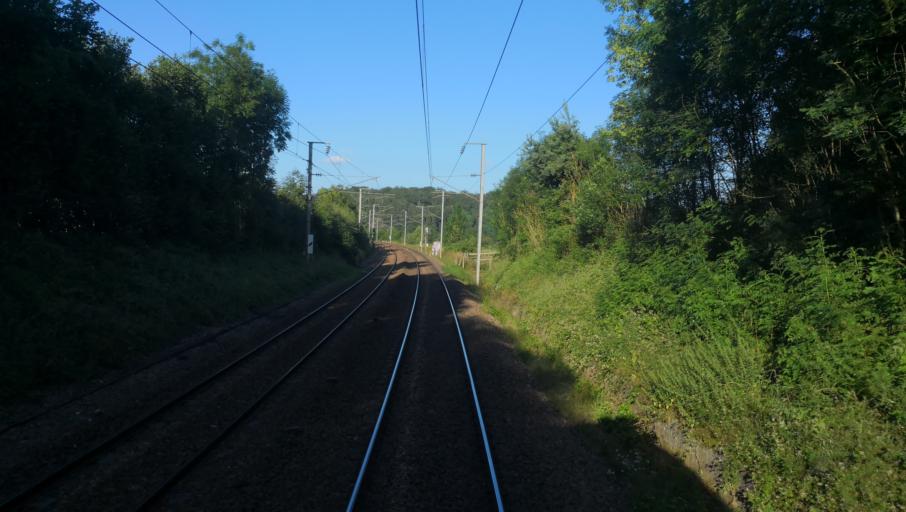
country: FR
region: Haute-Normandie
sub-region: Departement de l'Eure
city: Conches-en-Ouche
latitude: 48.9770
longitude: 1.0043
